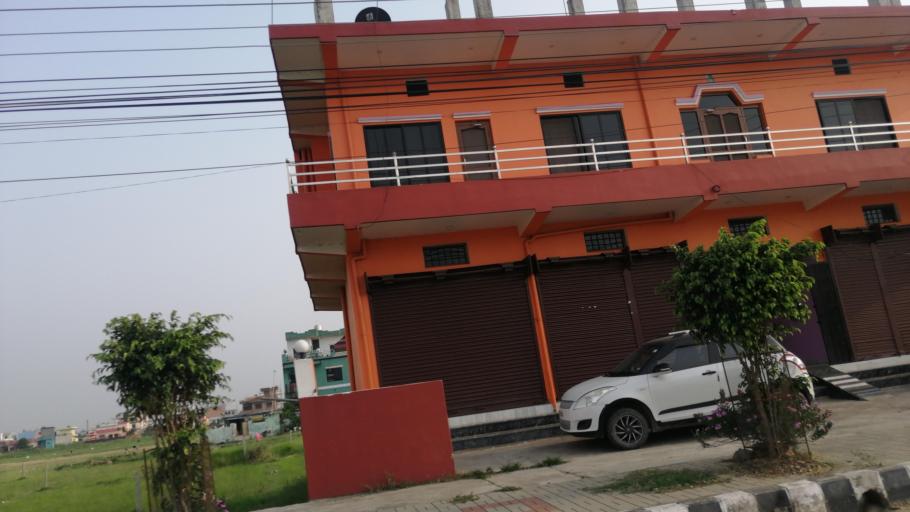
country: NP
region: Western Region
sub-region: Lumbini Zone
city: Bhairahawa
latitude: 27.4976
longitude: 83.4559
